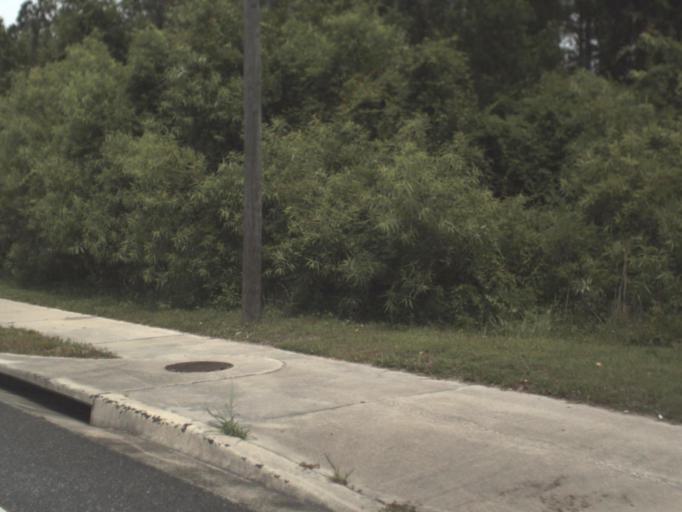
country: US
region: Florida
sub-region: Putnam County
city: Palatka
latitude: 29.6372
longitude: -81.7016
